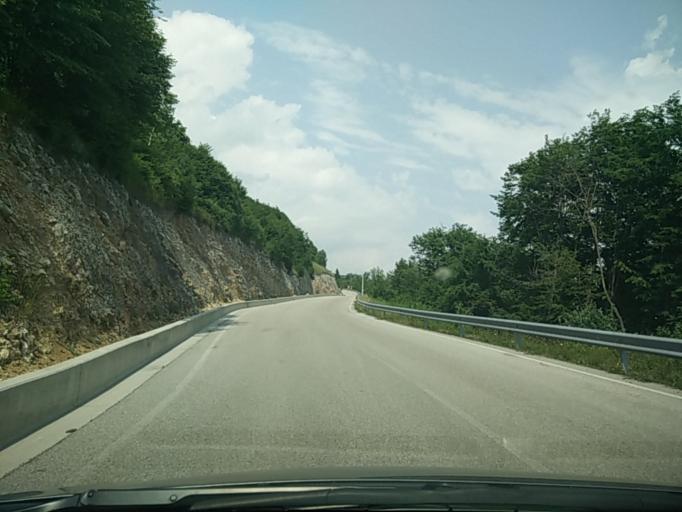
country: IT
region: Friuli Venezia Giulia
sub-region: Provincia di Pordenone
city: Budoia
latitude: 46.0790
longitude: 12.5392
